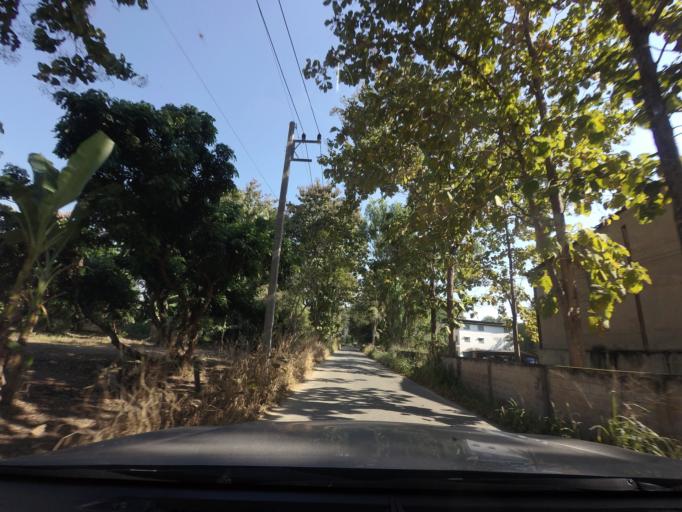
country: TH
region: Chiang Mai
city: San Kamphaeng
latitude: 18.7077
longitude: 99.1647
